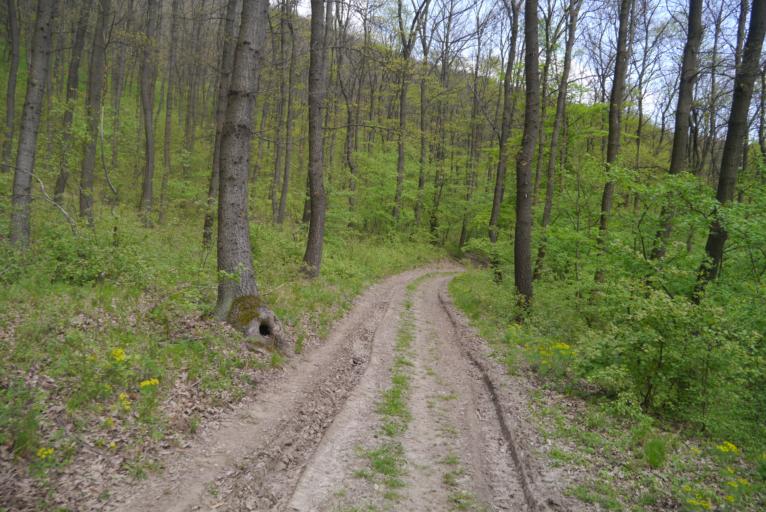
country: HU
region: Komarom-Esztergom
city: Piliscsev
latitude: 47.6920
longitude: 18.8437
